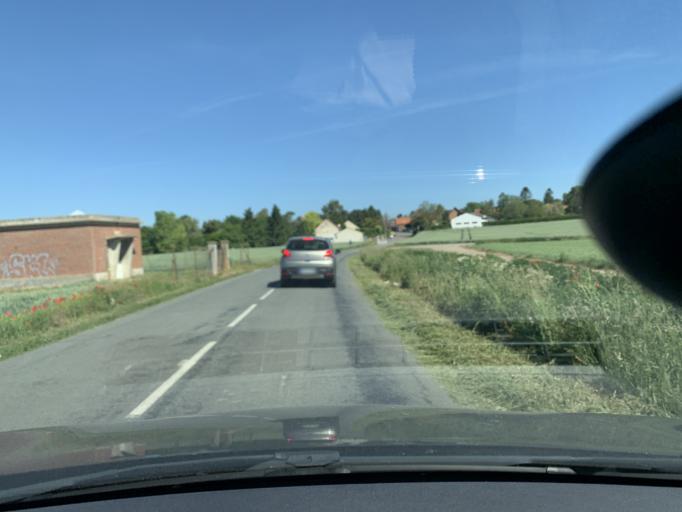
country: FR
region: Nord-Pas-de-Calais
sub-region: Departement du Nord
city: Fontaine-Notre-Dame
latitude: 50.1613
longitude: 3.1586
